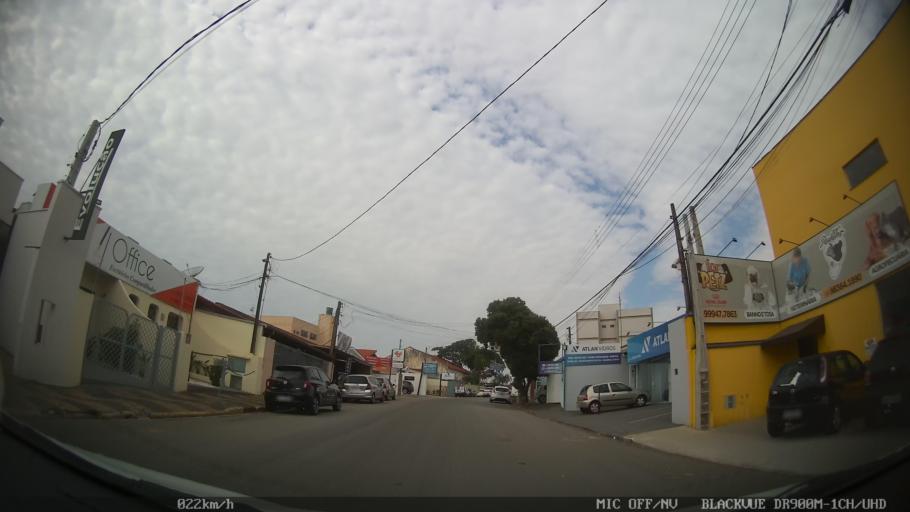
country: BR
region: Sao Paulo
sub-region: Paulinia
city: Paulinia
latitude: -22.7650
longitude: -47.1512
